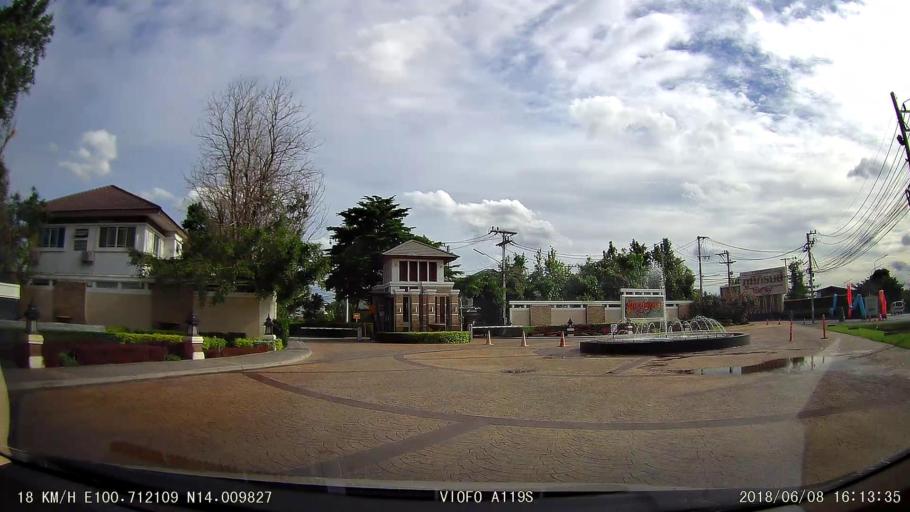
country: TH
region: Pathum Thani
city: Thanyaburi
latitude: 14.0097
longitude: 100.7122
